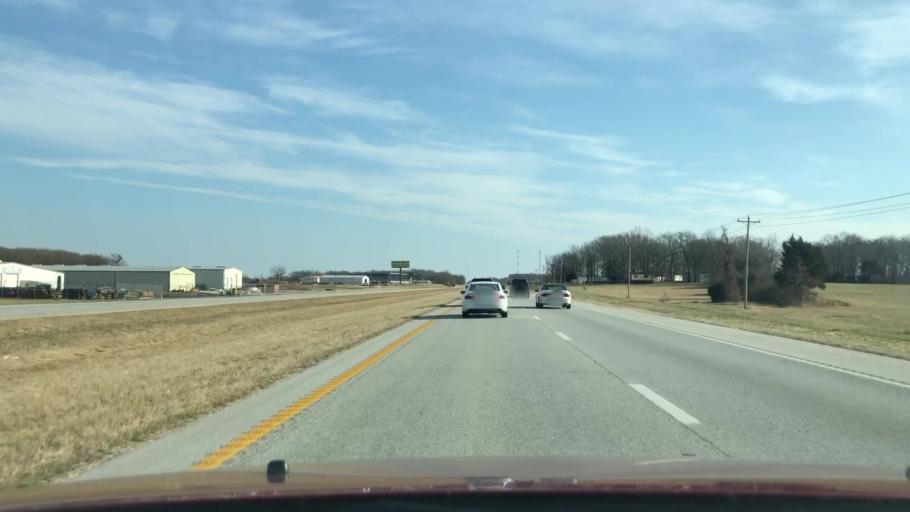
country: US
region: Missouri
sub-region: Webster County
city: Rogersville
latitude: 37.1140
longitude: -93.0375
